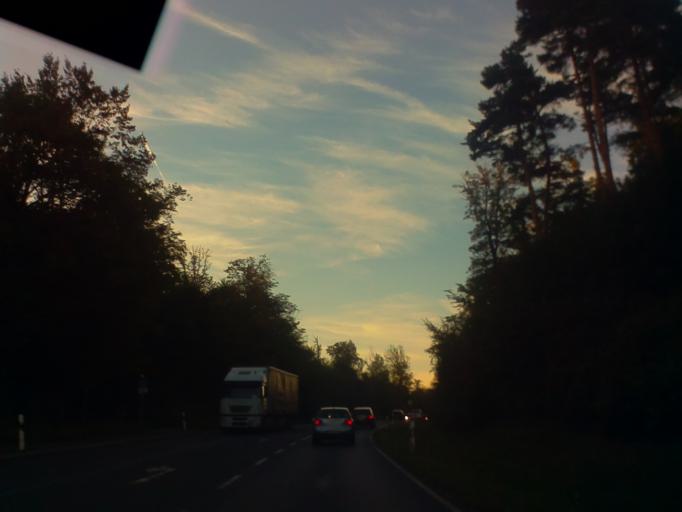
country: DE
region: Hesse
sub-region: Regierungsbezirk Darmstadt
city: Friedrichsdorf
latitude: 50.2756
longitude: 8.6655
